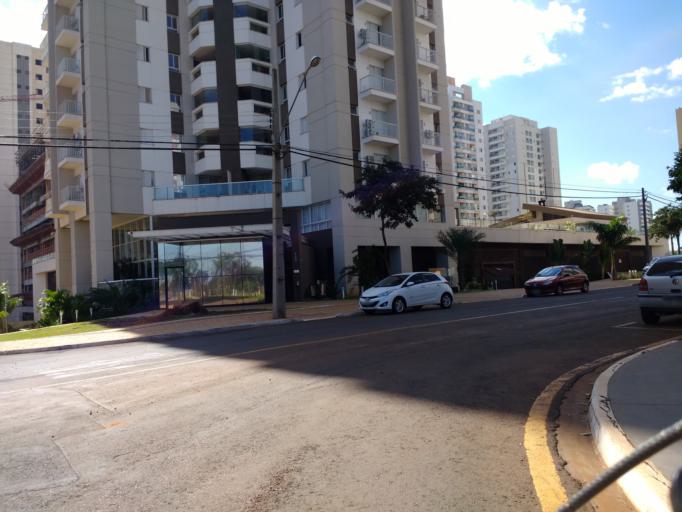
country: BR
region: Parana
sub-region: Londrina
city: Londrina
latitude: -23.3346
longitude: -51.1806
